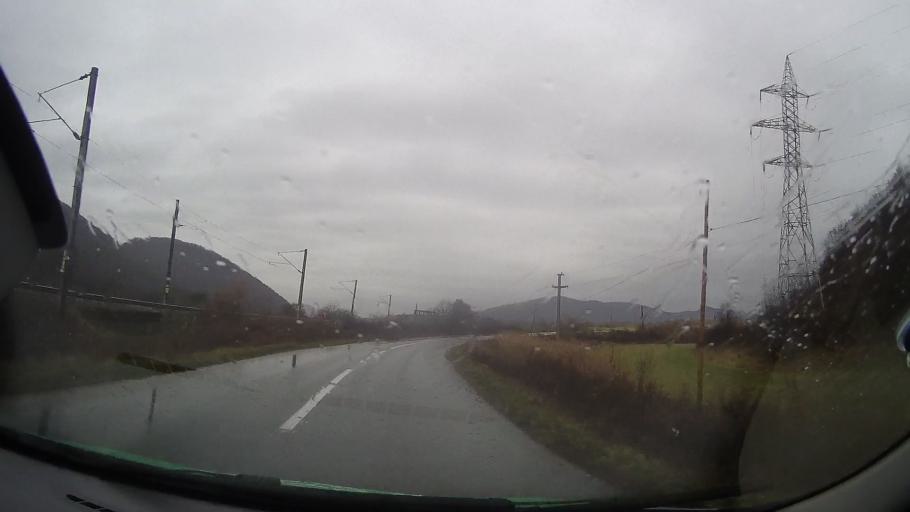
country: RO
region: Bistrita-Nasaud
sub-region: Municipiul Bistrita
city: Viisoara
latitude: 47.0506
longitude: 24.4521
